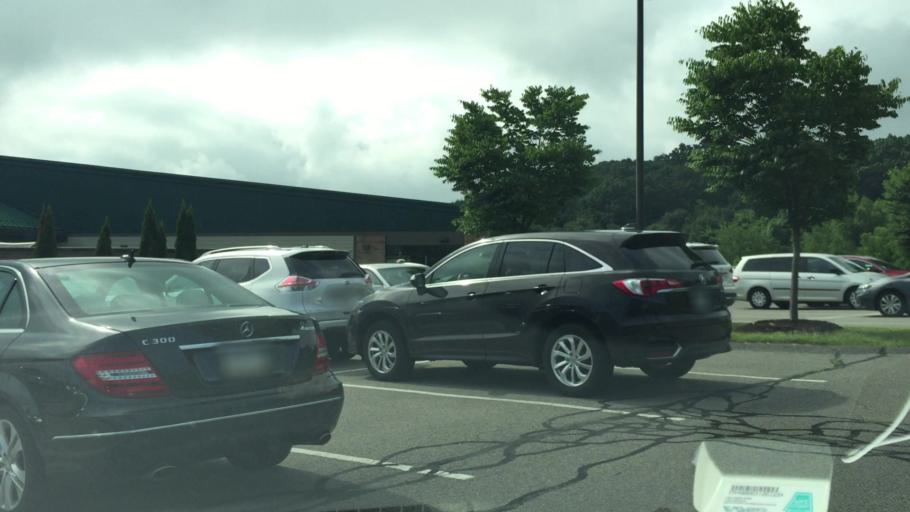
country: US
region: Pennsylvania
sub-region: Butler County
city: Seven Fields
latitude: 40.6614
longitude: -80.0426
